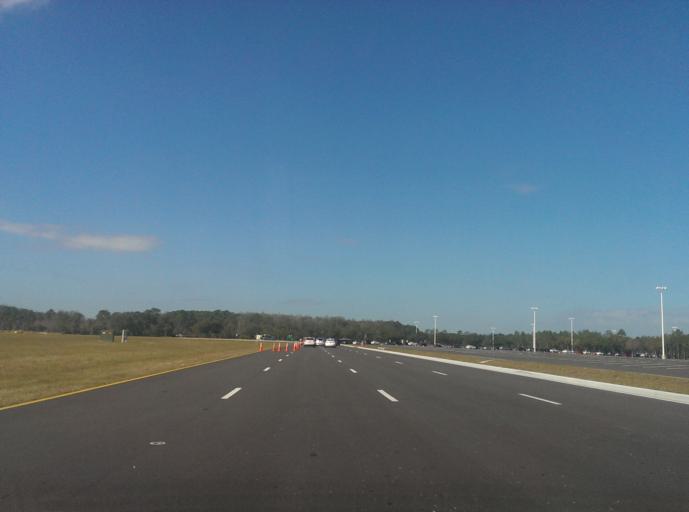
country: US
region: Florida
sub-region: Osceola County
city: Celebration
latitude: 28.3975
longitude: -81.5771
